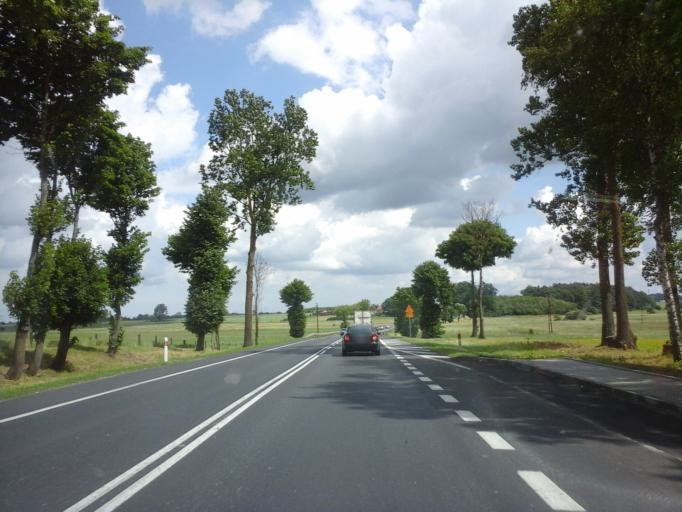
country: PL
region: West Pomeranian Voivodeship
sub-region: Powiat bialogardzki
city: Bialogard
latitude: 54.1208
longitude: 16.0096
